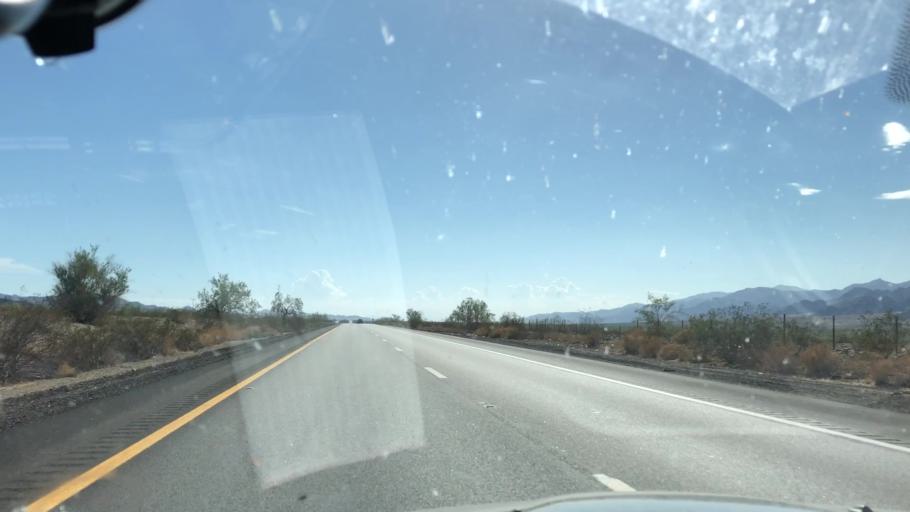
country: US
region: California
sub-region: Imperial County
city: Niland
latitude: 33.6962
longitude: -115.4820
